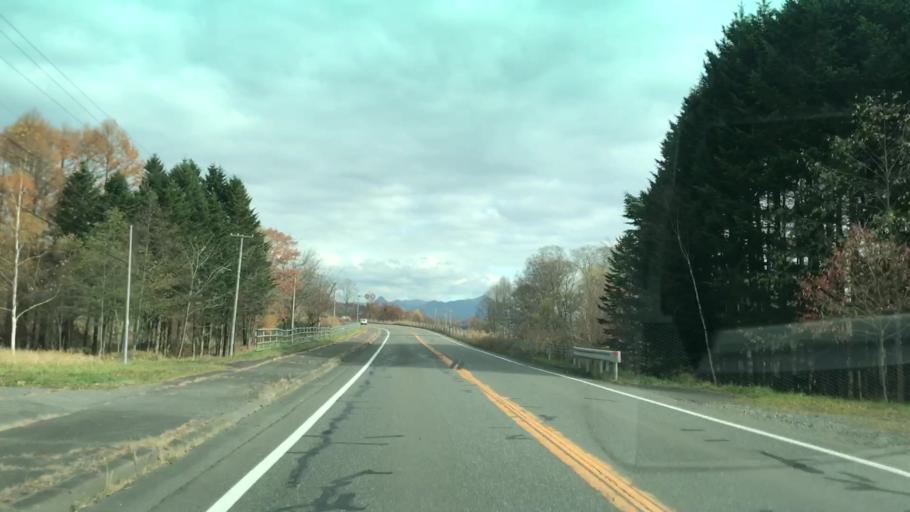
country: JP
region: Hokkaido
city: Shizunai-furukawacho
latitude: 42.7218
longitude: 142.2815
